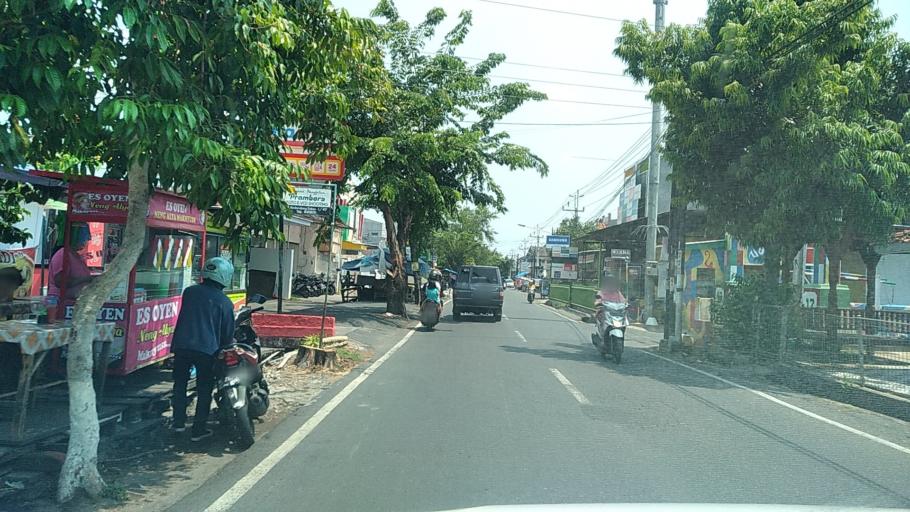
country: ID
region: Central Java
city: Semarang
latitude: -7.0082
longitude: 110.4425
